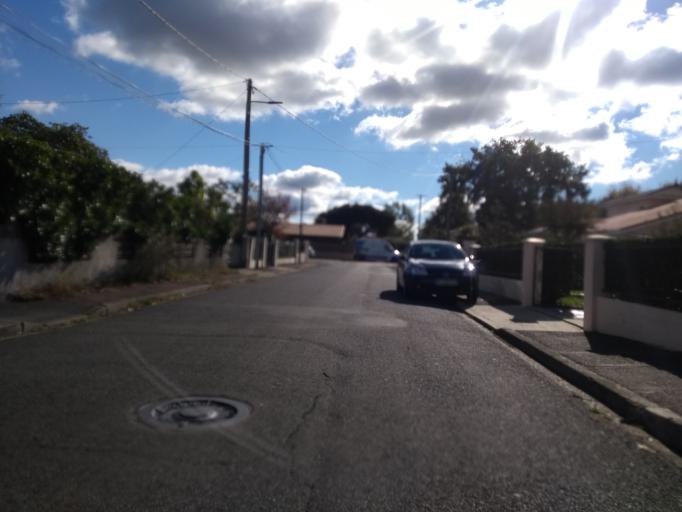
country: FR
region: Aquitaine
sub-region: Departement de la Gironde
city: Pessac
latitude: 44.8254
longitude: -0.6660
